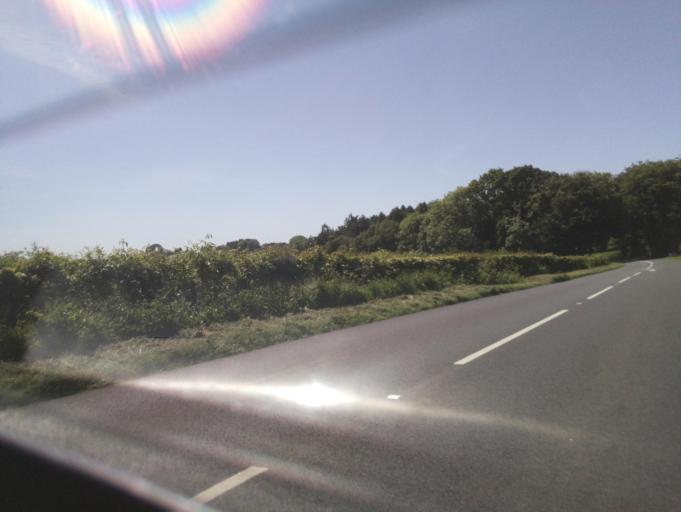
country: GB
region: England
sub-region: Devon
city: Honiton
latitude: 50.8641
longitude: -3.0965
